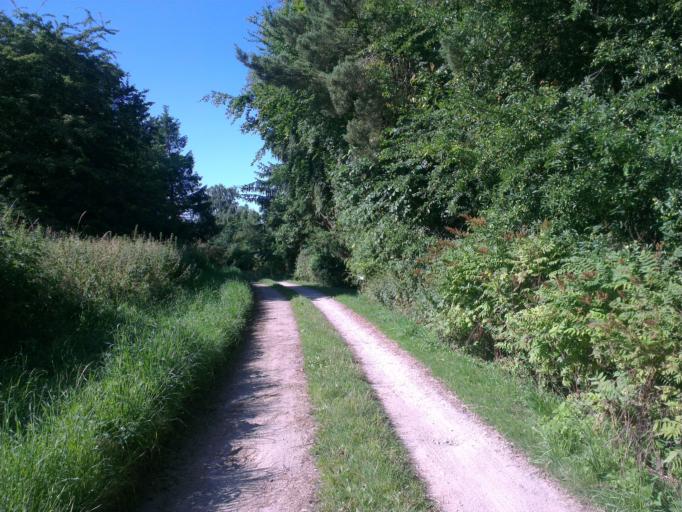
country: DK
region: Capital Region
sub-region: Frederikssund Kommune
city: Frederikssund
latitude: 55.7812
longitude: 12.0339
